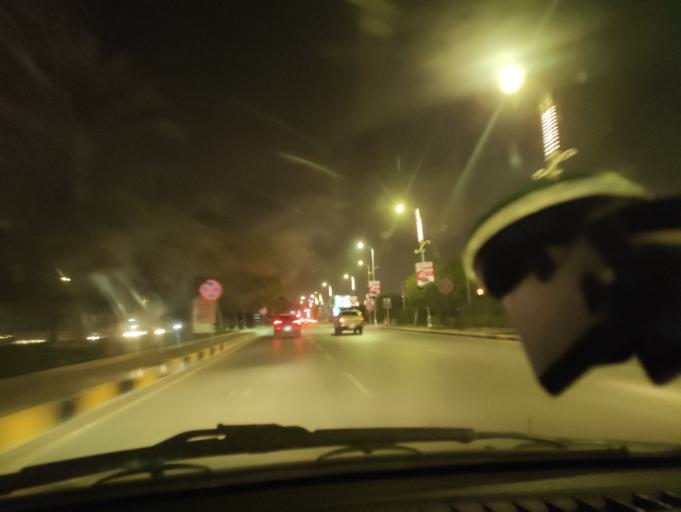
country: EG
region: Al Jizah
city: Awsim
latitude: 30.0204
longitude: 31.0067
